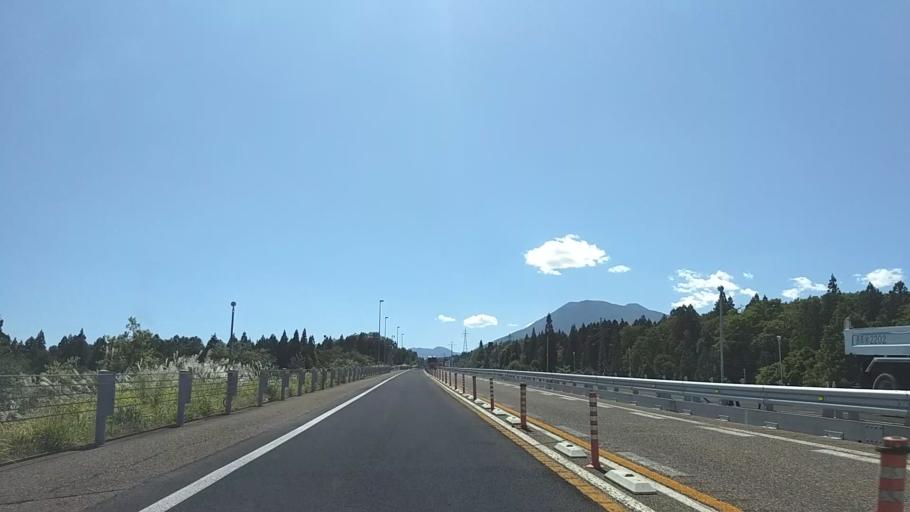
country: JP
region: Niigata
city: Arai
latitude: 36.8963
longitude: 138.2061
